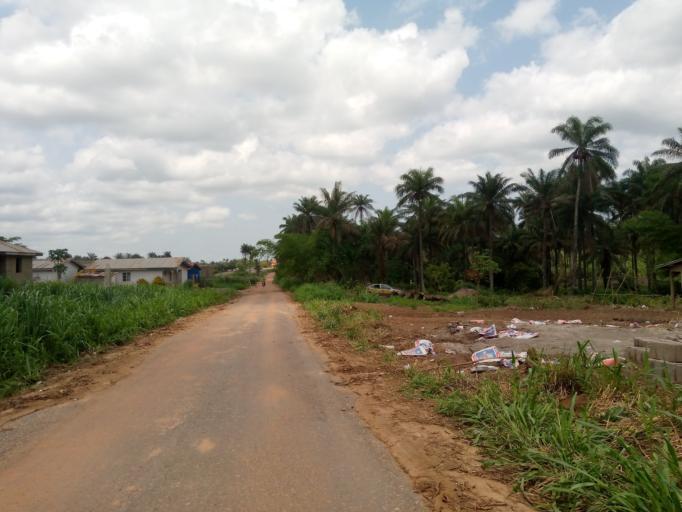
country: SL
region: Western Area
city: Waterloo
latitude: 8.3764
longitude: -12.9595
